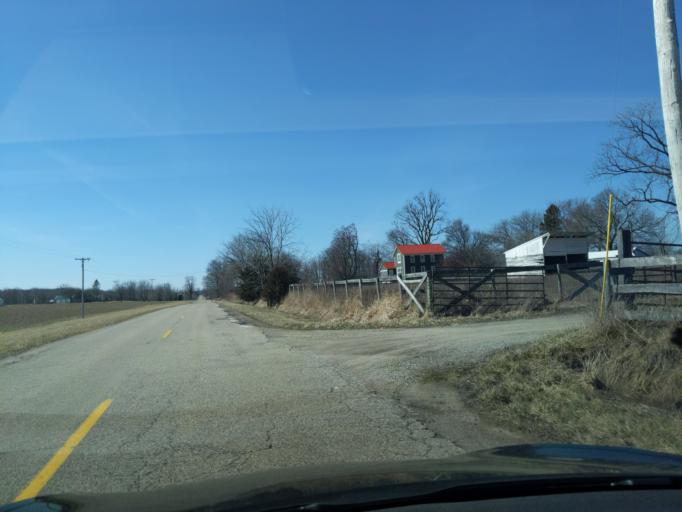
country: US
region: Michigan
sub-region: Ionia County
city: Portland
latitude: 42.7267
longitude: -84.9507
